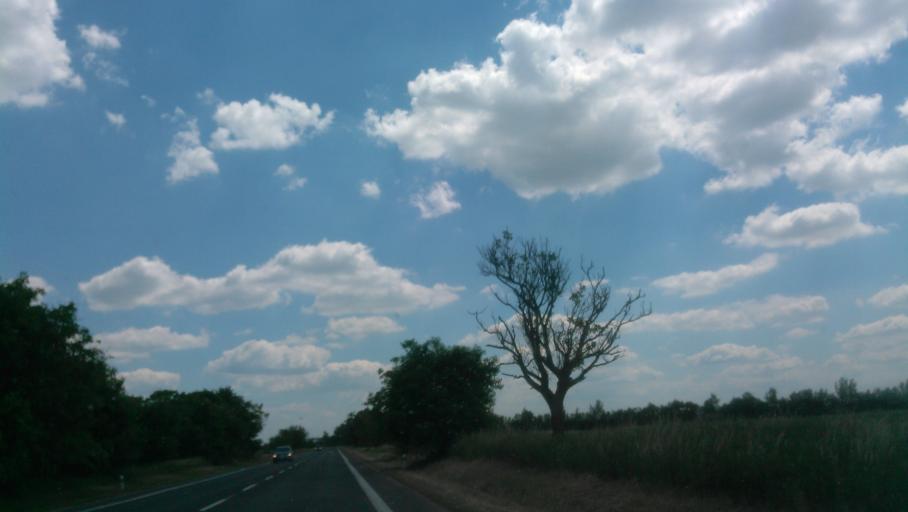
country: SK
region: Trnavsky
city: Samorin
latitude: 48.0484
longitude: 17.2926
